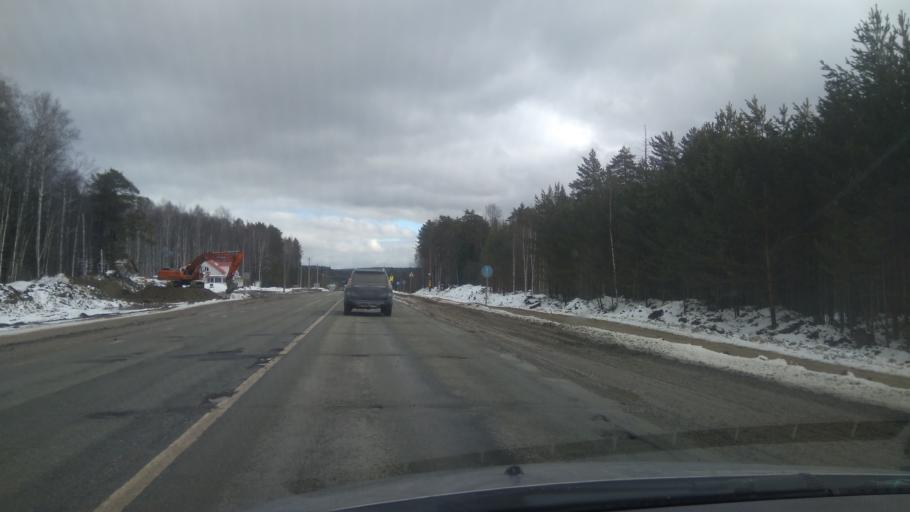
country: RU
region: Sverdlovsk
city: Bisert'
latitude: 56.8323
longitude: 58.9481
